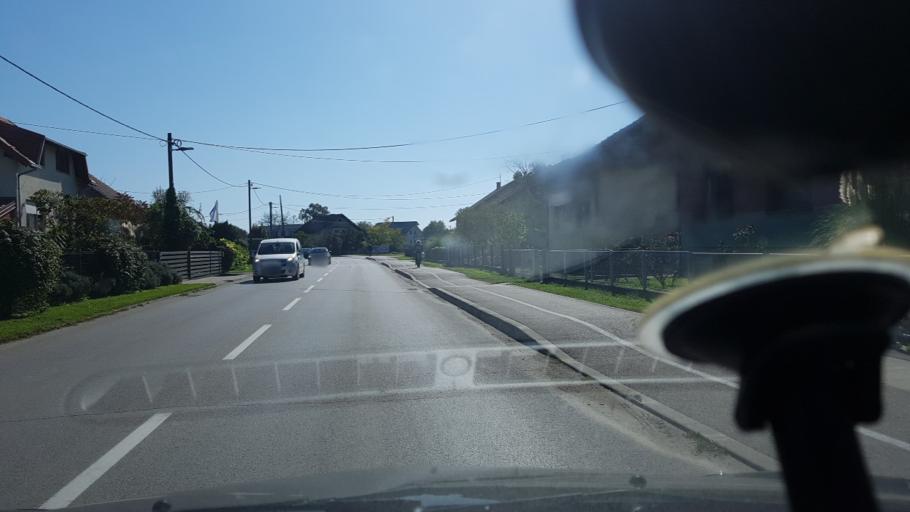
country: HR
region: Zagrebacka
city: Lupoglav
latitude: 45.7020
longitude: 16.3954
